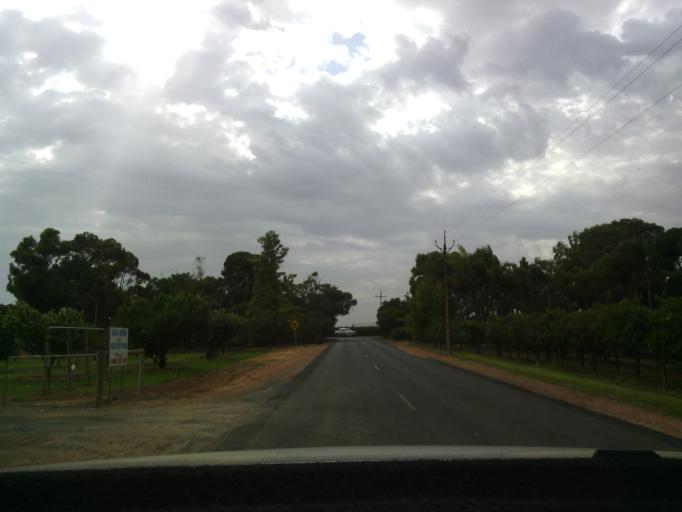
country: AU
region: South Australia
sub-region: Berri and Barmera
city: Monash
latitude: -34.2637
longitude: 140.5738
